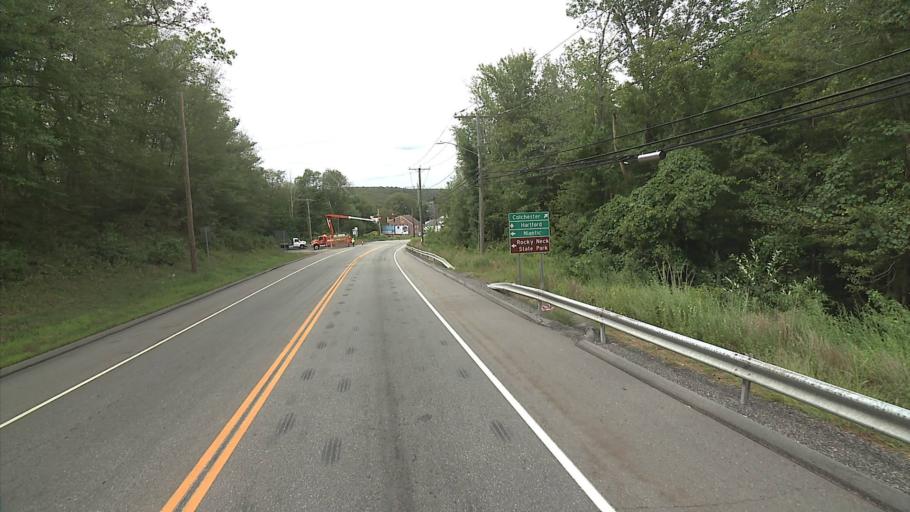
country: US
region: Connecticut
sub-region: New London County
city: Montville Center
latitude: 41.4273
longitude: -72.2139
